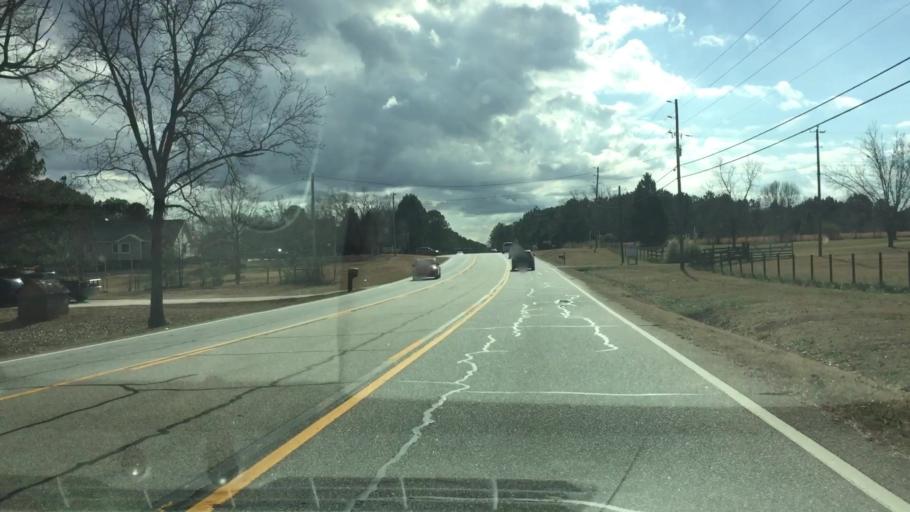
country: US
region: Georgia
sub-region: Henry County
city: McDonough
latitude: 33.4952
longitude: -84.1450
